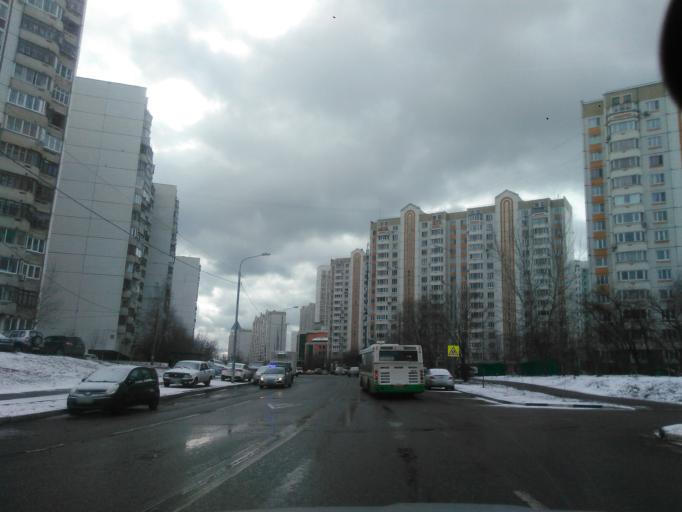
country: RU
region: Moskovskaya
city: Krasnogorsk
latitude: 55.8481
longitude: 37.3440
